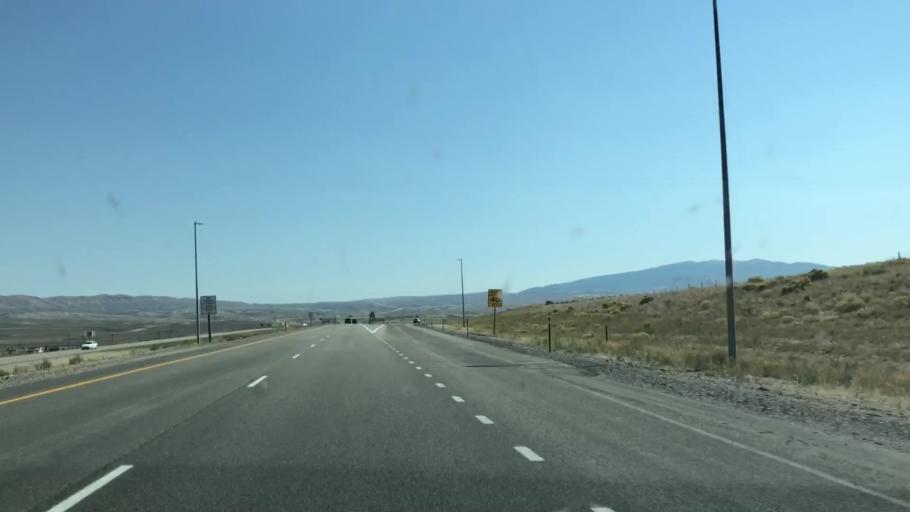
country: US
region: Wyoming
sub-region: Carbon County
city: Saratoga
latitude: 41.7410
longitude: -106.8396
